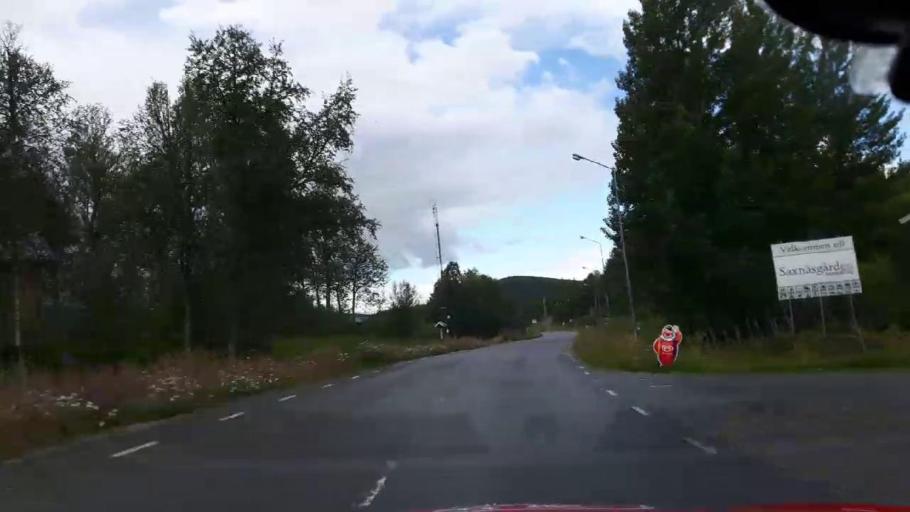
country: SE
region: Vaesterbotten
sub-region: Vilhelmina Kommun
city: Sjoberg
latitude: 64.9701
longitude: 15.3595
